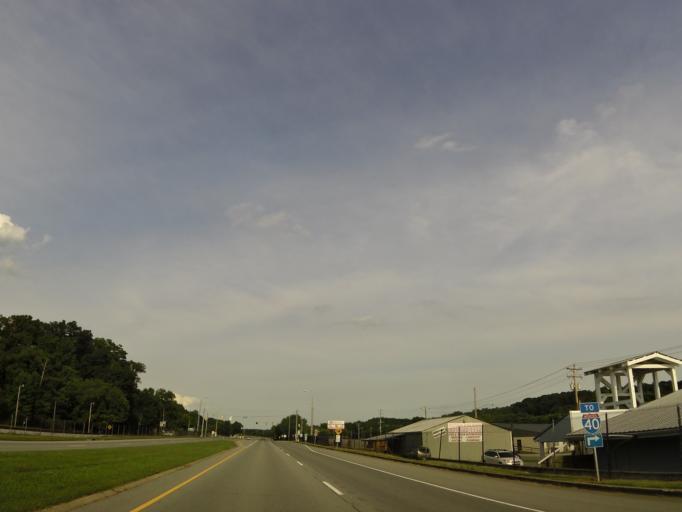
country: US
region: Tennessee
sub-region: Humphreys County
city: Waverly
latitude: 36.0866
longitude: -87.7910
